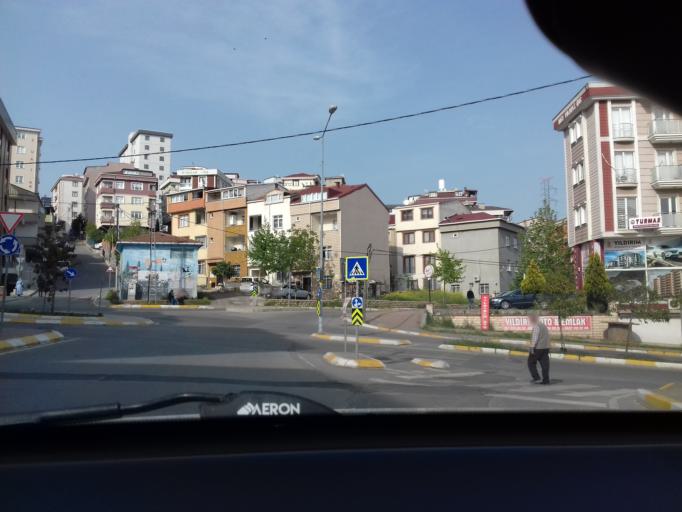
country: TR
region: Istanbul
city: Pendik
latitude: 40.9116
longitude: 29.2785
